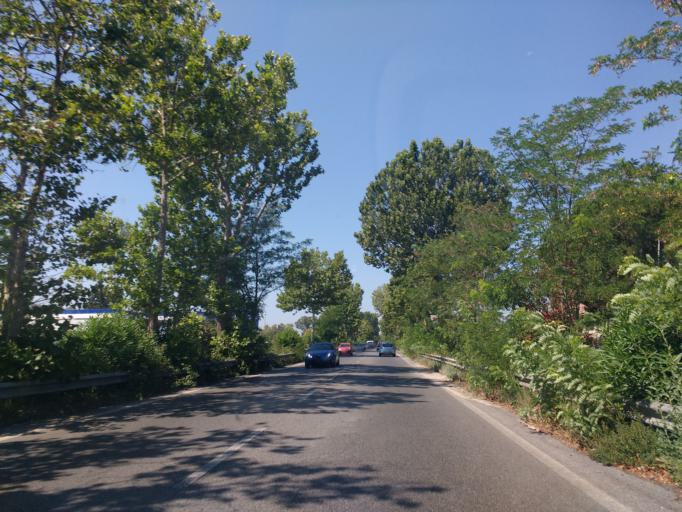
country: IT
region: Latium
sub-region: Citta metropolitana di Roma Capitale
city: Acilia-Castel Fusano-Ostia Antica
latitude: 41.7658
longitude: 12.3148
